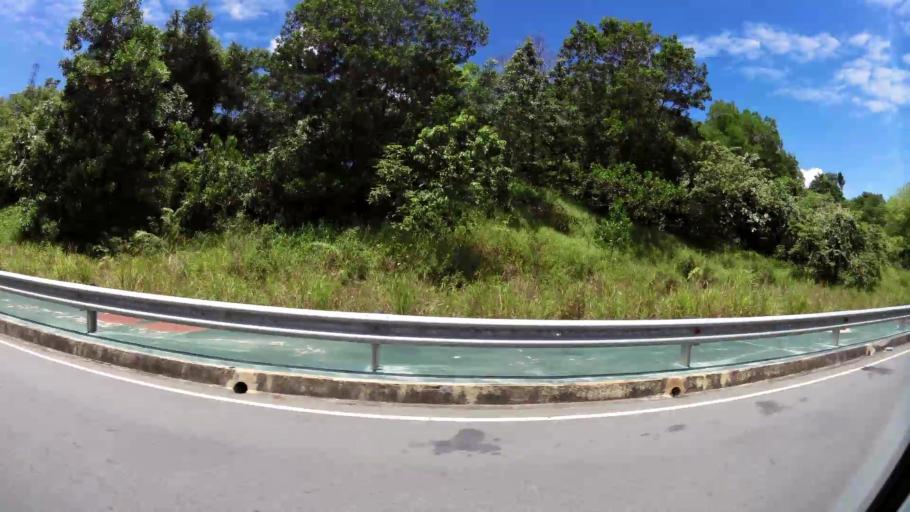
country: BN
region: Brunei and Muara
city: Bandar Seri Begawan
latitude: 5.0031
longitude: 115.0145
